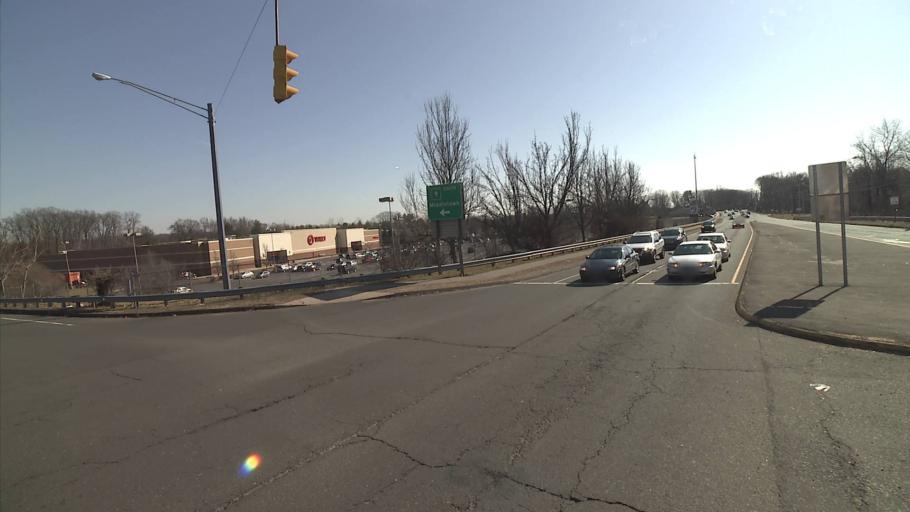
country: US
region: Connecticut
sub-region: Hartford County
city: Newington
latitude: 41.7123
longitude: -72.7649
